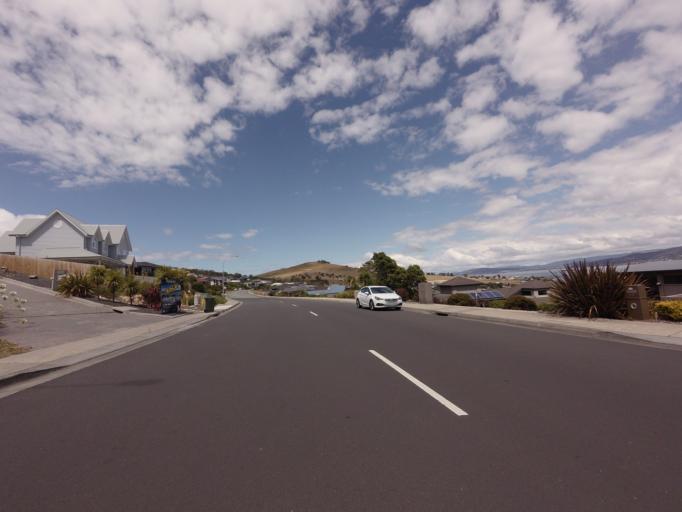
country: AU
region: Tasmania
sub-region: Clarence
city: Howrah
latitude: -42.9089
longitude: 147.4209
